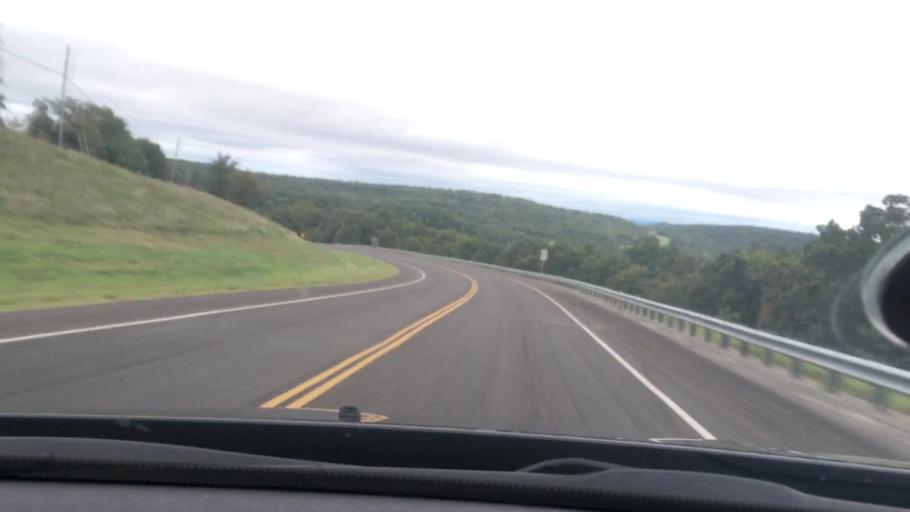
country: US
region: Oklahoma
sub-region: Sequoyah County
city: Vian
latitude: 35.5470
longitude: -94.9699
